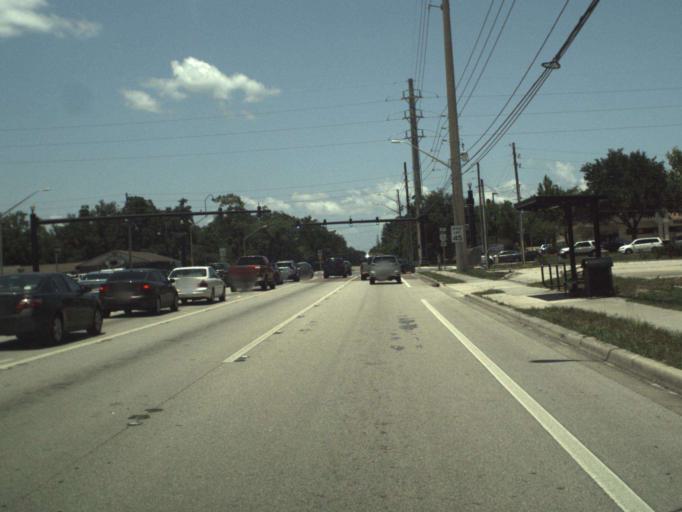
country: US
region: Florida
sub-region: Seminole County
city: Oviedo
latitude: 28.6547
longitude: -81.2081
